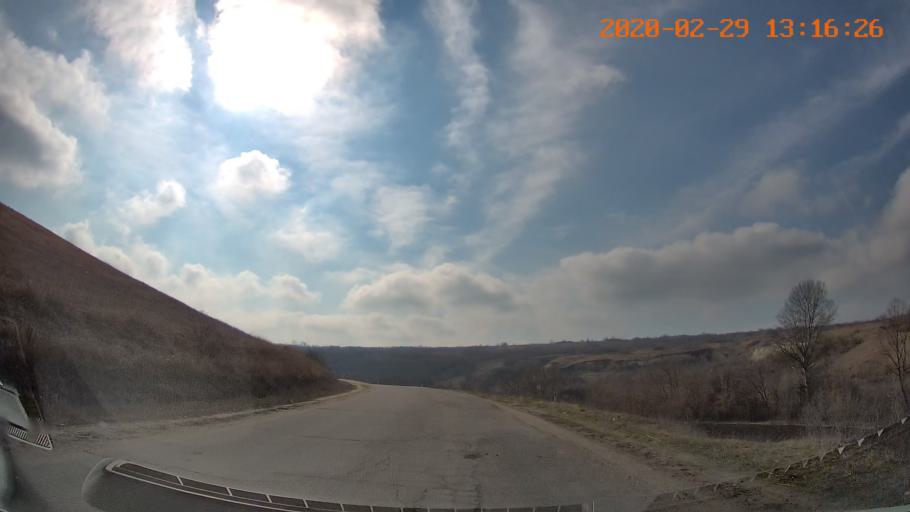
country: MD
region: Telenesti
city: Camenca
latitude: 48.0027
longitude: 28.6638
